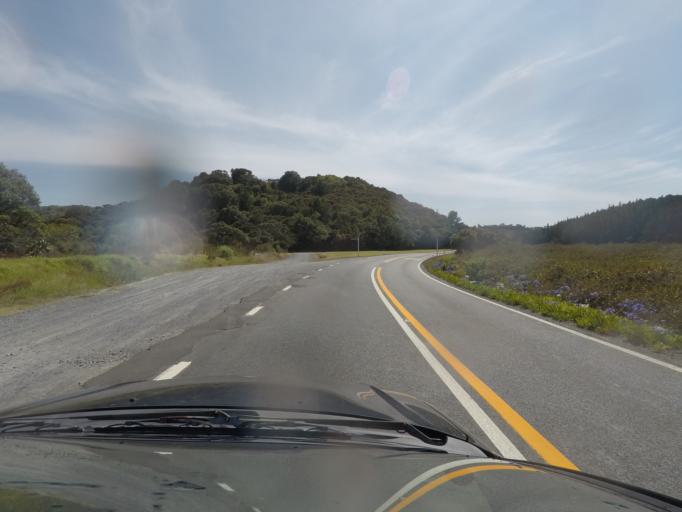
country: NZ
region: Auckland
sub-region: Auckland
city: Warkworth
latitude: -36.3081
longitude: 174.7786
